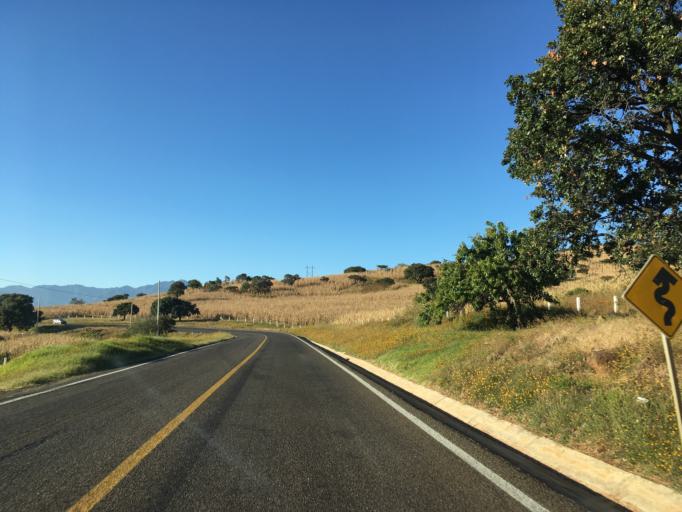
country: MX
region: Michoacan
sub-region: Tuxpan
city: La Soledad
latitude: 19.5007
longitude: -100.4619
